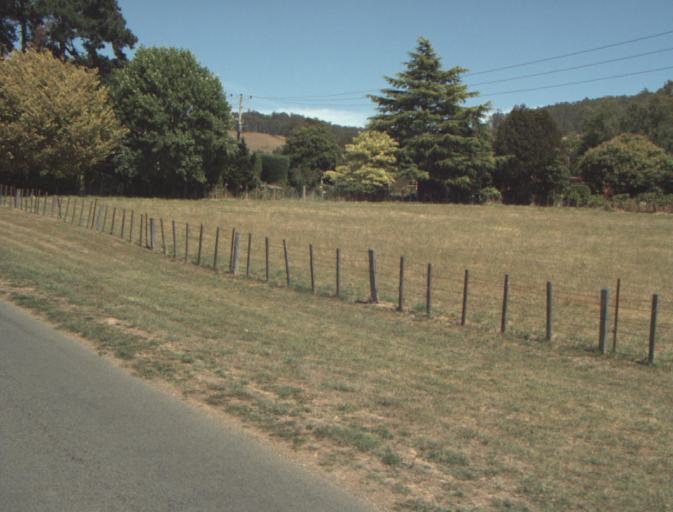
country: AU
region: Tasmania
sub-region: Launceston
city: Mayfield
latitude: -41.2627
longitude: 147.1352
